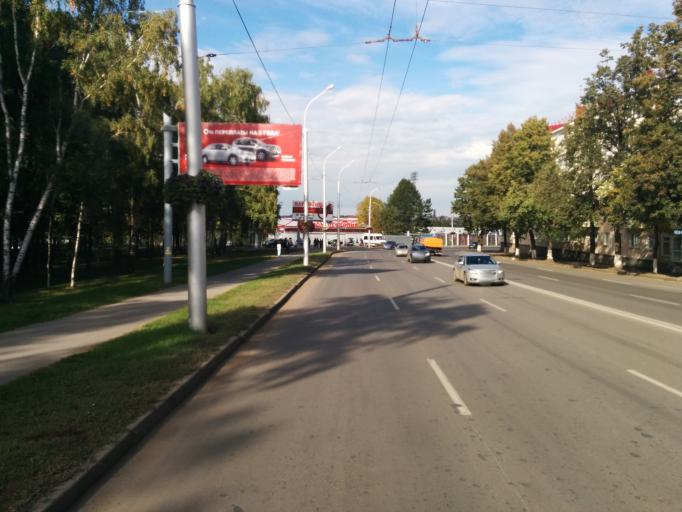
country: RU
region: Bashkortostan
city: Ufa
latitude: 54.8234
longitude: 56.0598
